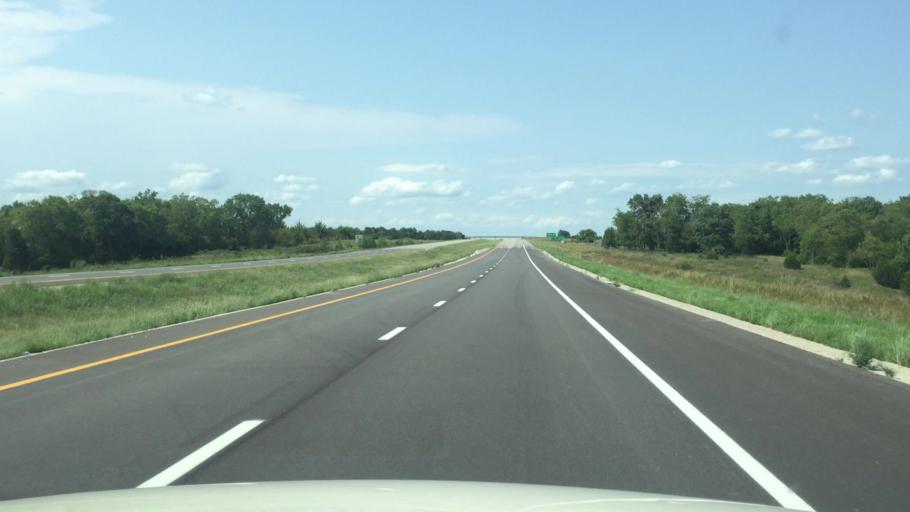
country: US
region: Kansas
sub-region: Linn County
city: La Cygne
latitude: 38.3870
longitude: -94.6874
